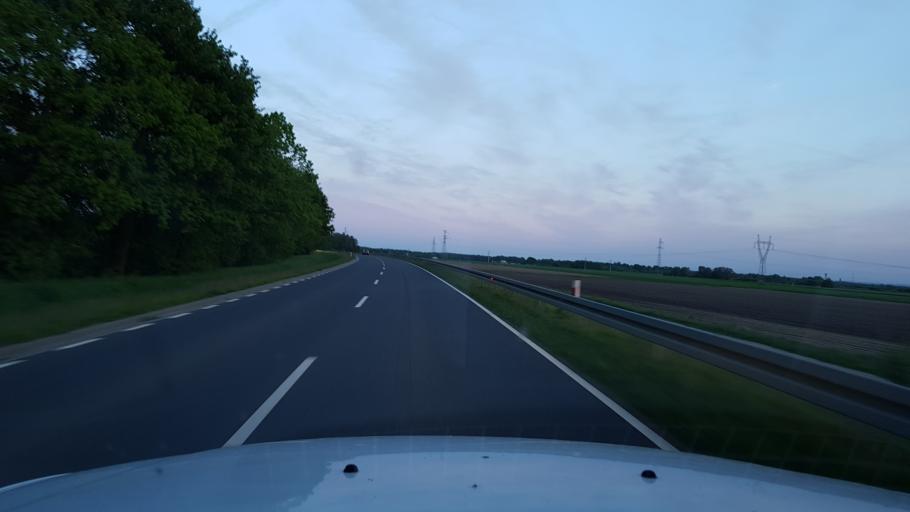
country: PL
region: West Pomeranian Voivodeship
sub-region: Powiat goleniowski
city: Goleniow
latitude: 53.5810
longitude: 14.8682
